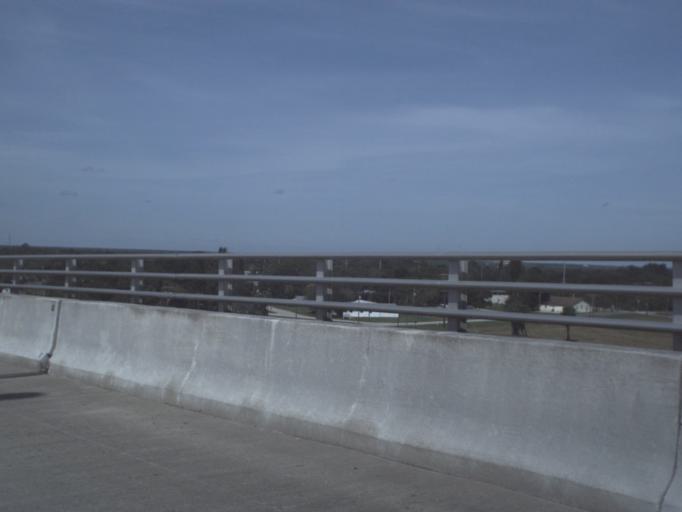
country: US
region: Florida
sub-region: Glades County
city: Moore Haven
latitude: 26.8336
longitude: -81.0897
